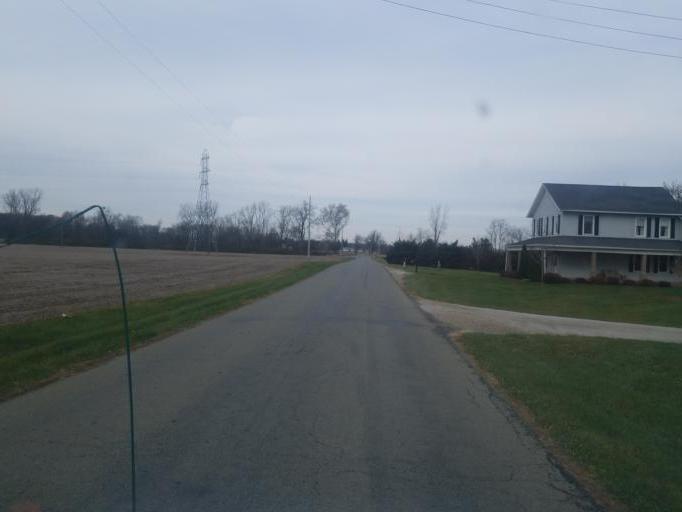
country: US
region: Ohio
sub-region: Knox County
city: Mount Vernon
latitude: 40.4076
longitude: -82.5124
